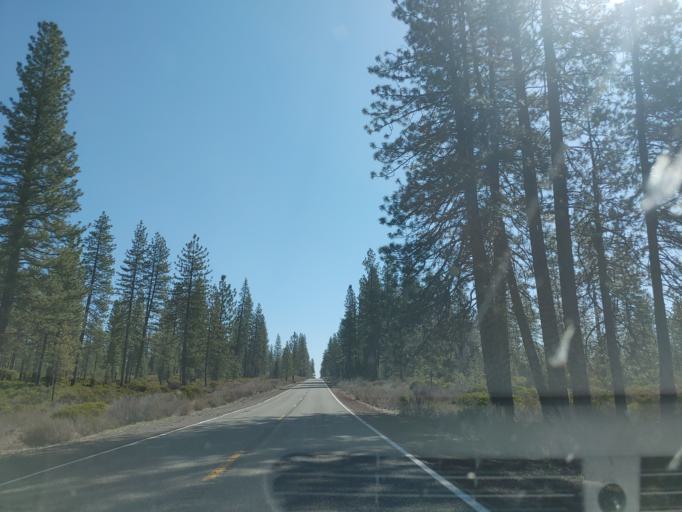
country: US
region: California
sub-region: Siskiyou County
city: McCloud
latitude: 41.2556
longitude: -122.0501
